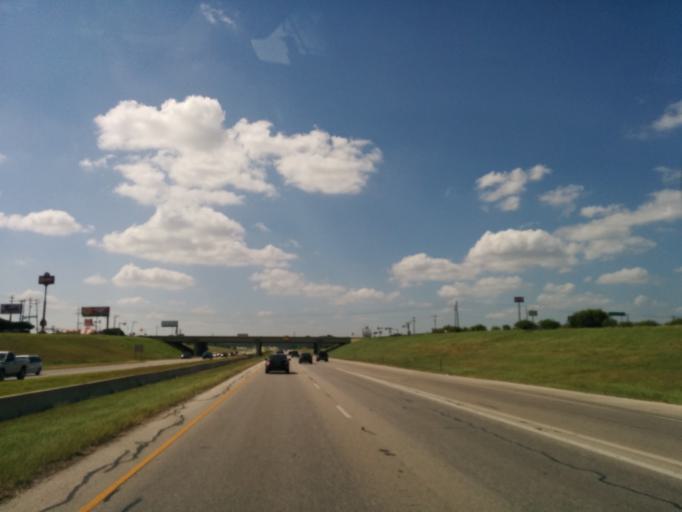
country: US
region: Texas
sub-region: Bexar County
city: Live Oak
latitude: 29.5899
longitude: -98.3505
